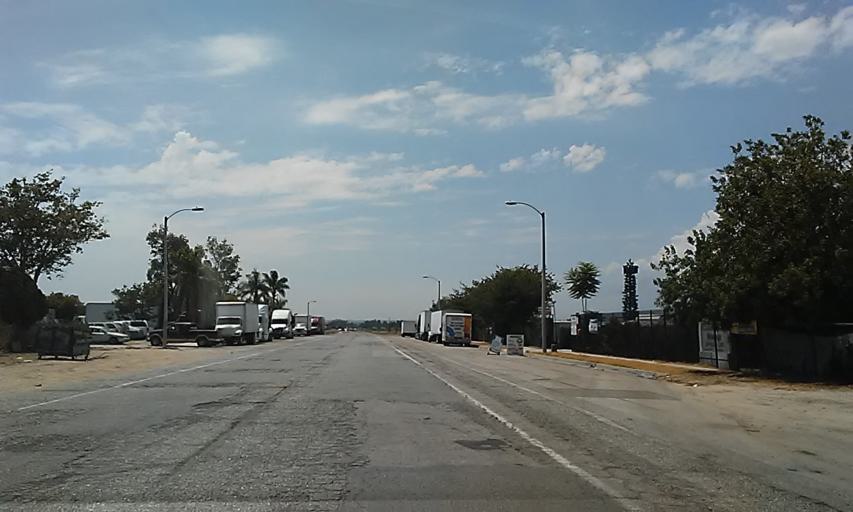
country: US
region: California
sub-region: San Bernardino County
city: Highland
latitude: 34.1084
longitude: -117.2353
